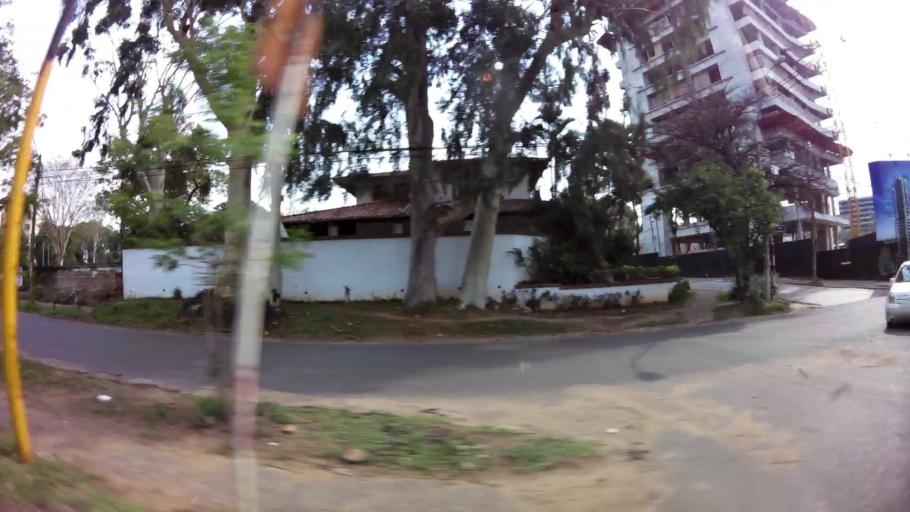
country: PY
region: Central
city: Fernando de la Mora
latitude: -25.2855
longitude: -57.5596
